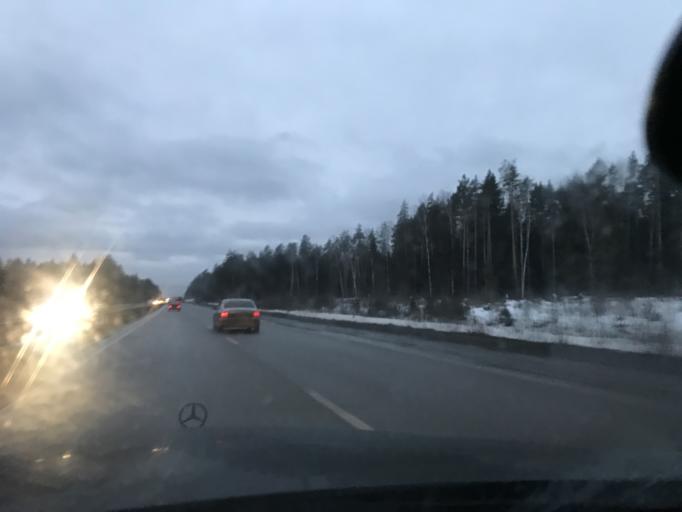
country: RU
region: Vladimir
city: Petushki
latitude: 55.9315
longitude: 39.3710
